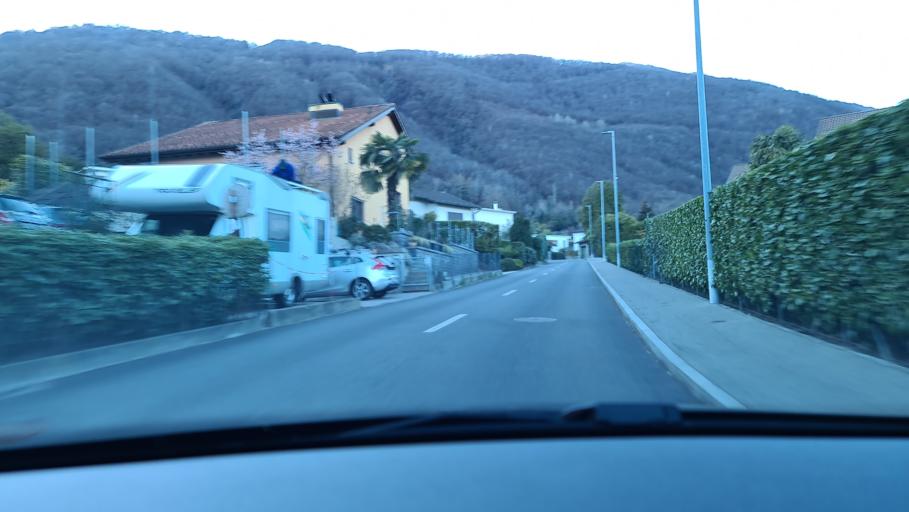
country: CH
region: Ticino
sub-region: Lugano District
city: Gravesano
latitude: 46.0416
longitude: 8.9206
